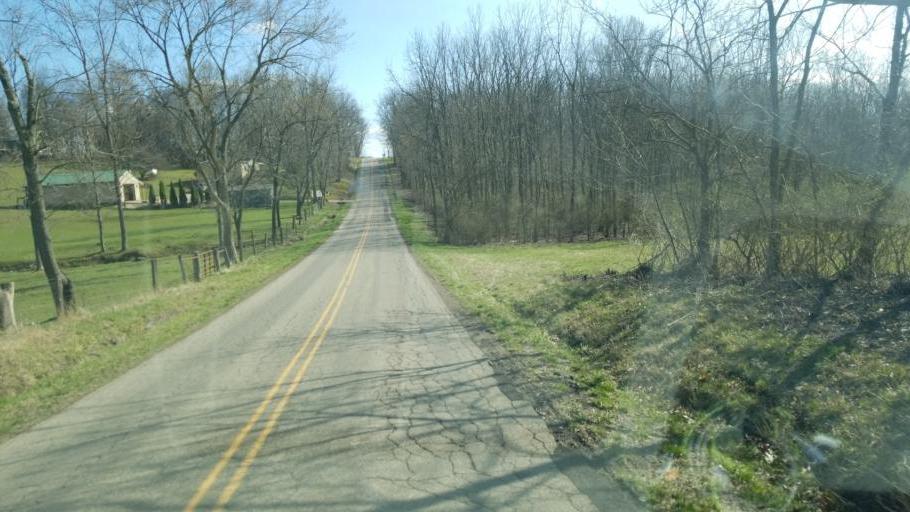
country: US
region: Ohio
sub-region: Licking County
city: Utica
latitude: 40.2561
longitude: -82.3221
